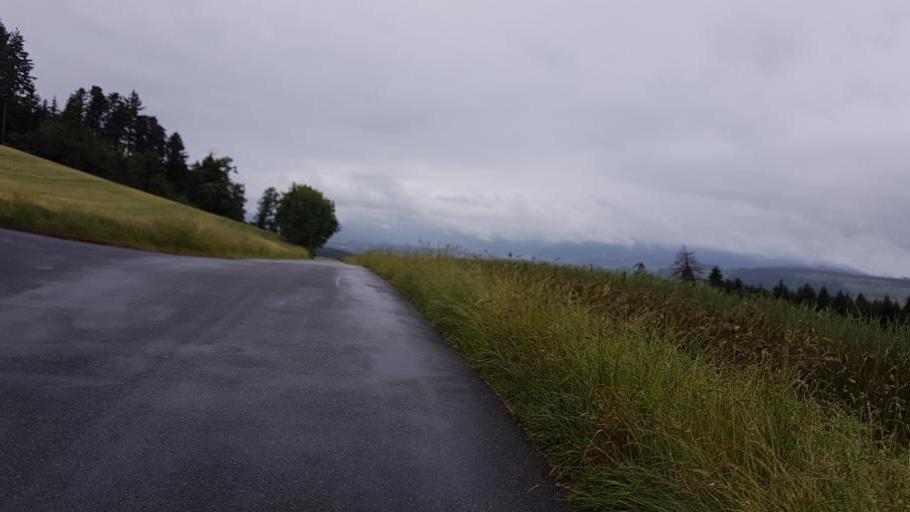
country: CH
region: Bern
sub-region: Bern-Mittelland District
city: Taegertschi
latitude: 46.8858
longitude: 7.5913
